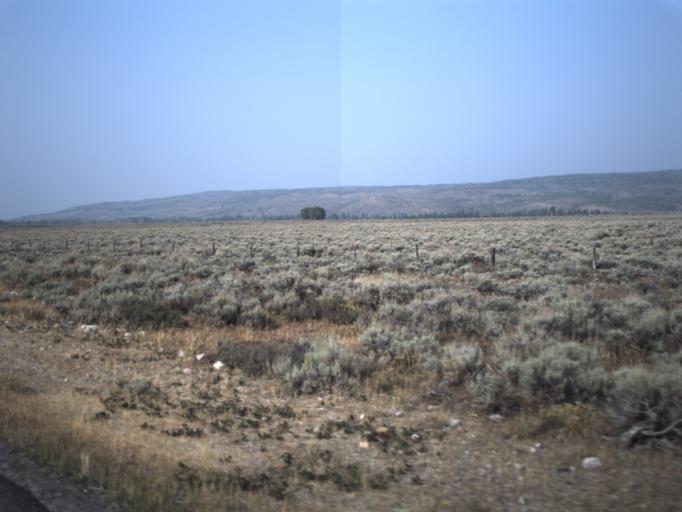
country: US
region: Wyoming
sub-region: Uinta County
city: Evanston
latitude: 40.9537
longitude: -110.8421
